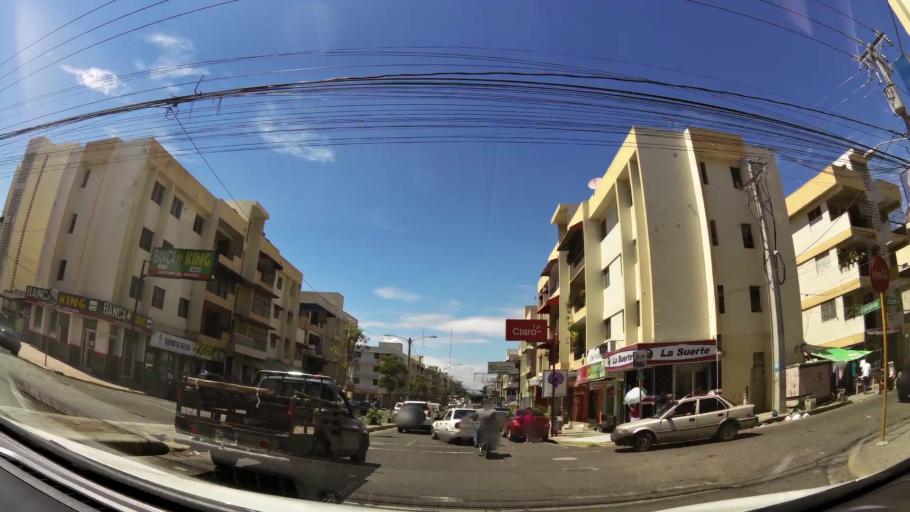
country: DO
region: Santiago
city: Santiago de los Caballeros
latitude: 19.4537
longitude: -70.6994
